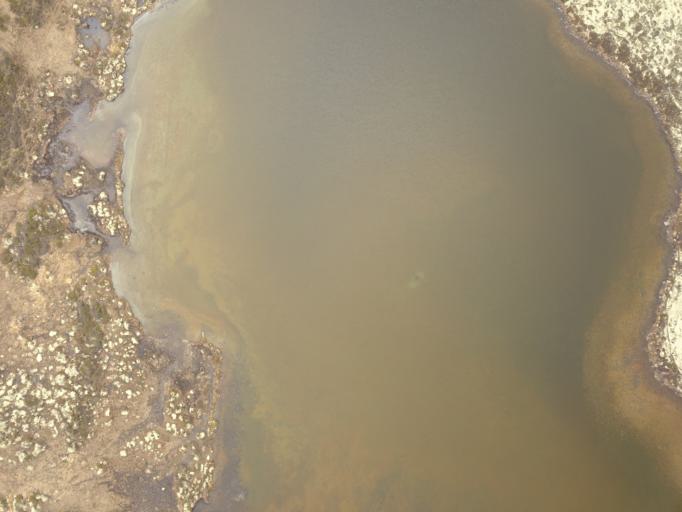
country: NO
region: Hedmark
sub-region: Folldal
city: Folldal
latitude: 62.2286
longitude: 9.6451
